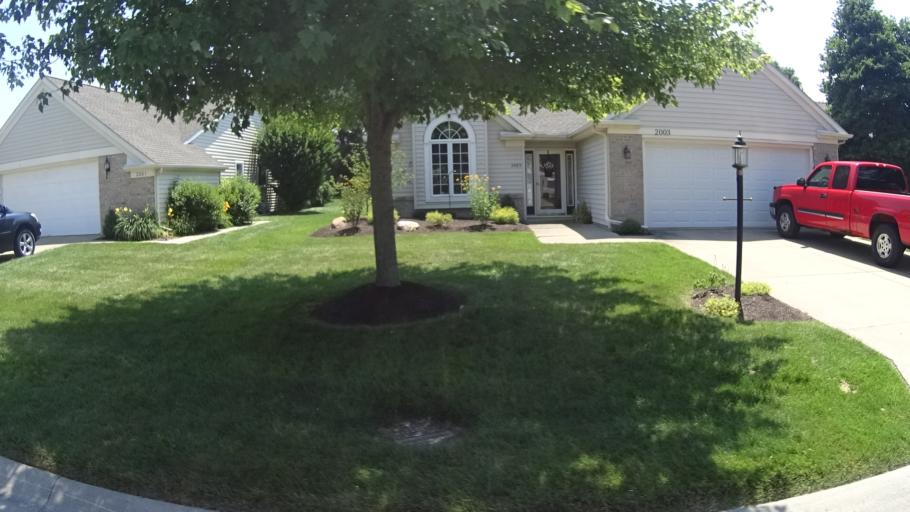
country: US
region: Ohio
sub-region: Erie County
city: Sandusky
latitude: 41.4052
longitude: -82.6526
